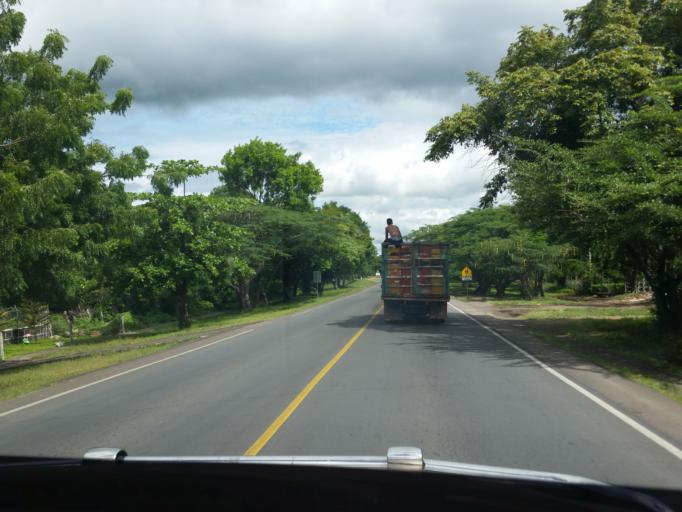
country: NI
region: Matagalpa
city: Ciudad Dario
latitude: 12.7716
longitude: -86.1246
